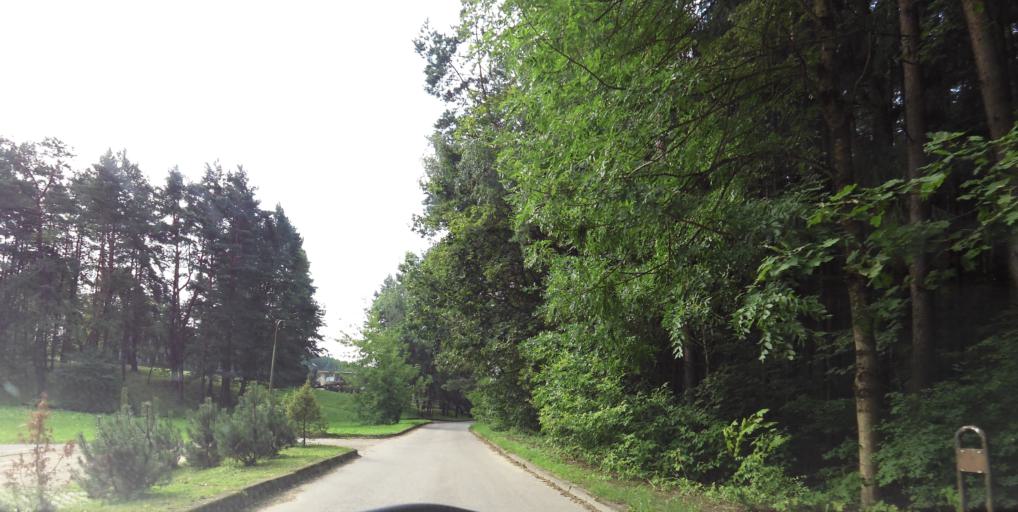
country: LT
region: Vilnius County
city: Seskine
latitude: 54.7311
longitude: 25.2841
